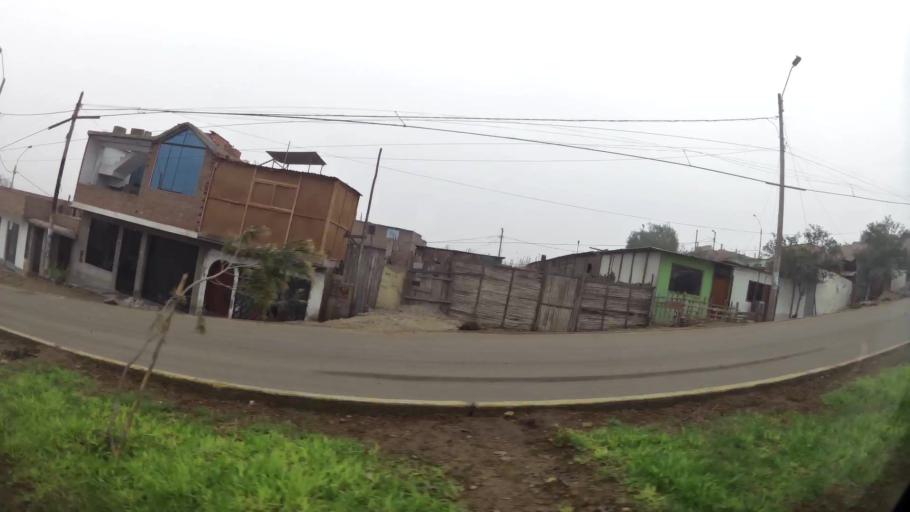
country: PE
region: Lima
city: Ventanilla
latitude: -11.8320
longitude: -77.1064
